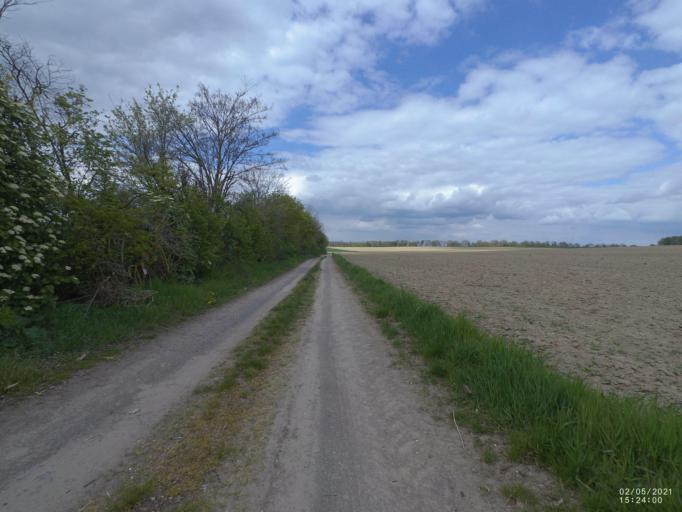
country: DE
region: Rheinland-Pfalz
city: Saffig
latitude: 50.3571
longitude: 7.4346
